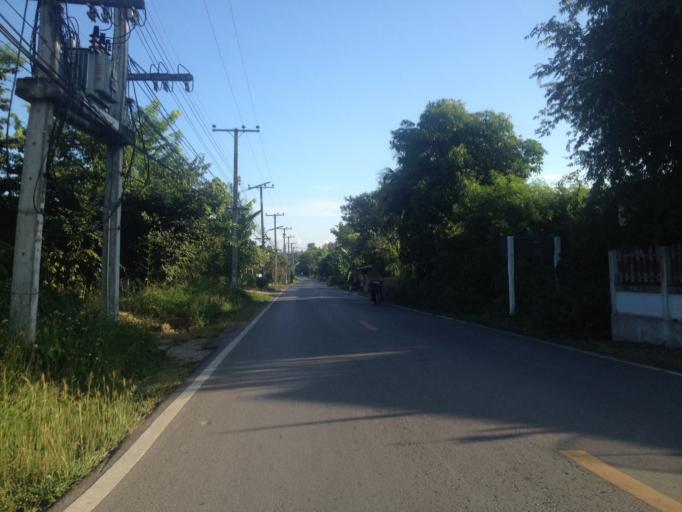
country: TH
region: Chiang Mai
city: San Pa Tong
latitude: 18.5729
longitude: 98.8674
